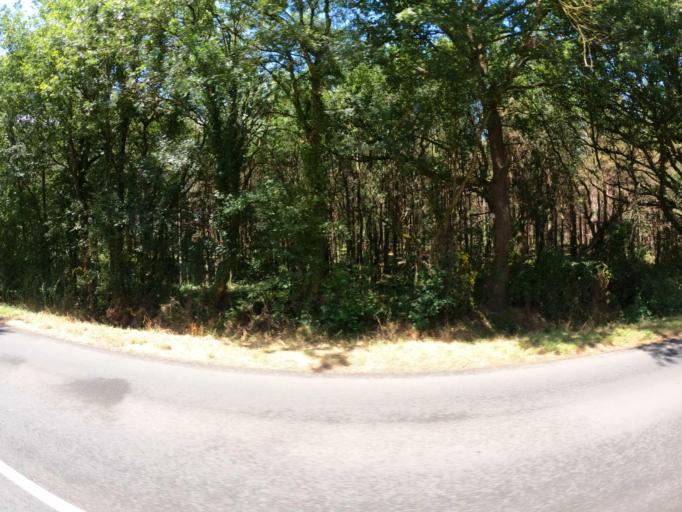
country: FR
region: Pays de la Loire
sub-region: Departement de Maine-et-Loire
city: Champigne
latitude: 47.6336
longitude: -0.5802
